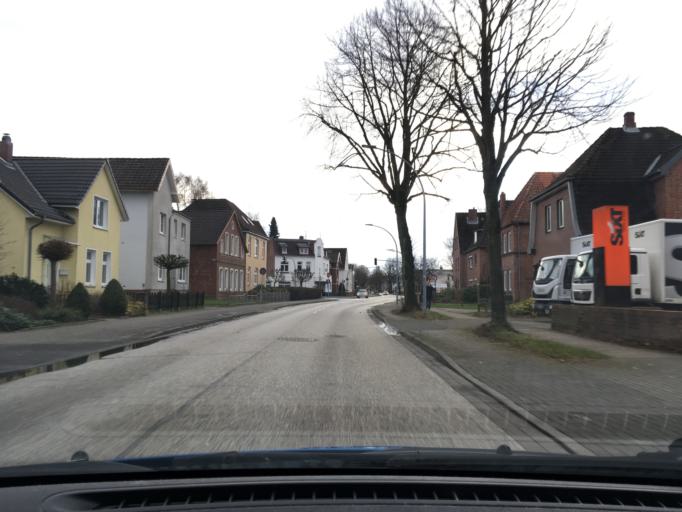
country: DE
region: Schleswig-Holstein
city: Itzehoe
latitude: 53.9359
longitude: 9.5010
